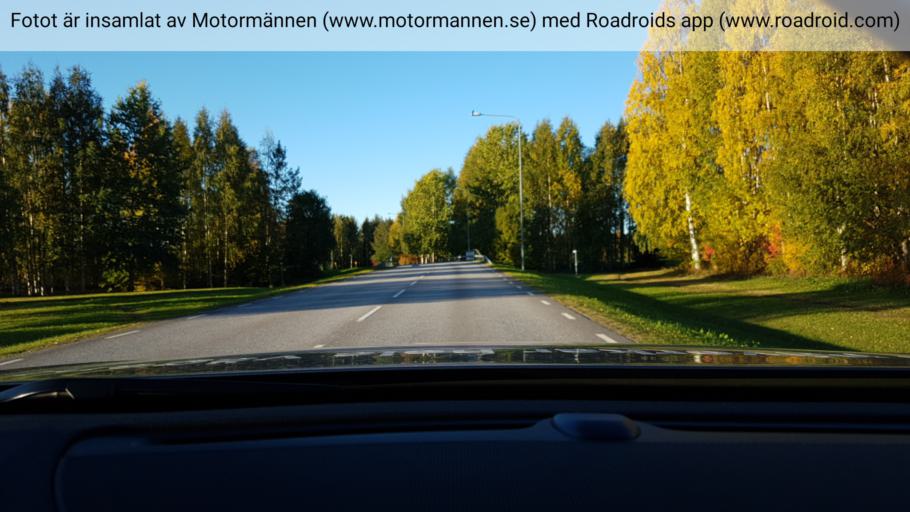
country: SE
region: Norrbotten
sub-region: Lulea Kommun
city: Sodra Sunderbyn
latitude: 65.6569
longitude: 21.9482
